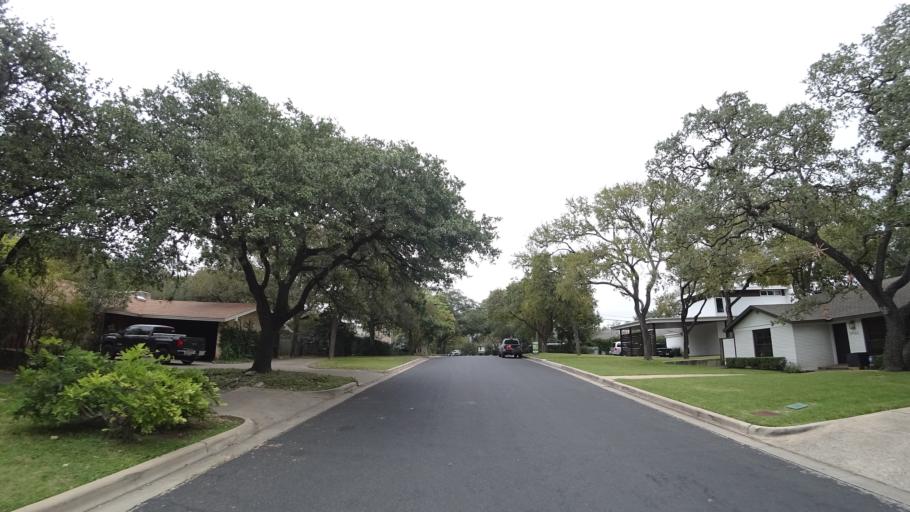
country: US
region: Texas
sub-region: Travis County
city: West Lake Hills
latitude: 30.3065
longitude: -97.7722
